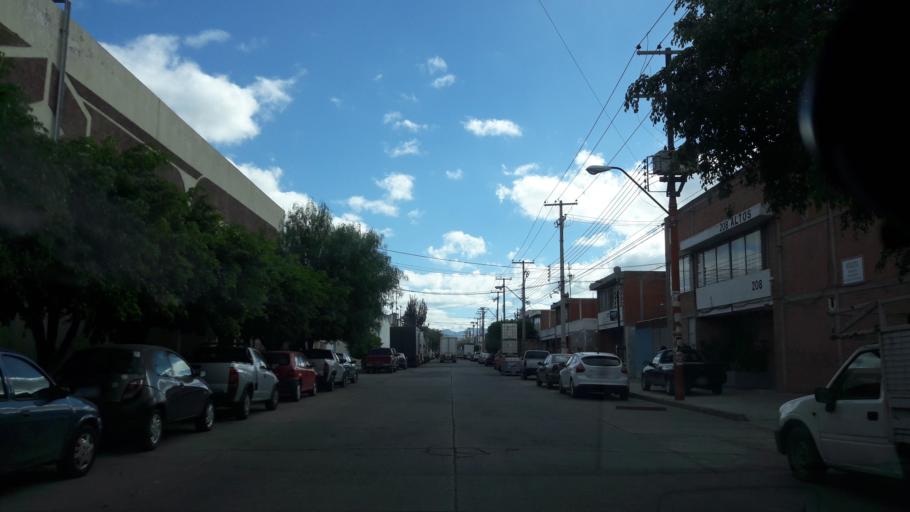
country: MX
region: Guanajuato
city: Leon
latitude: 21.1023
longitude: -101.6326
